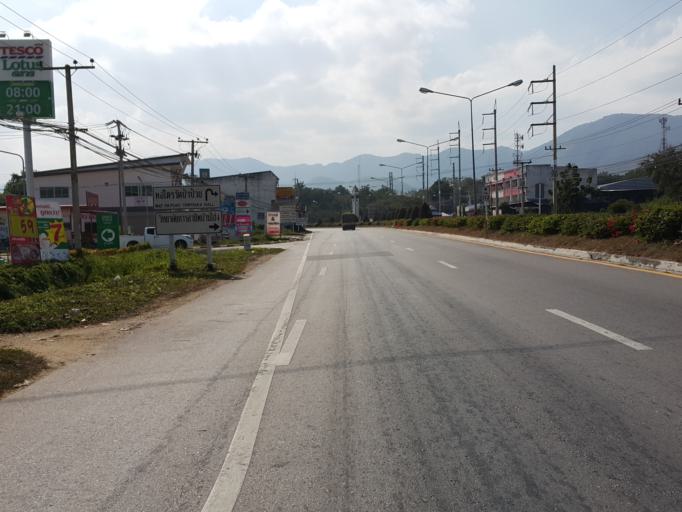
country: TH
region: Lamphun
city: Ban Hong
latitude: 18.3018
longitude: 98.8170
